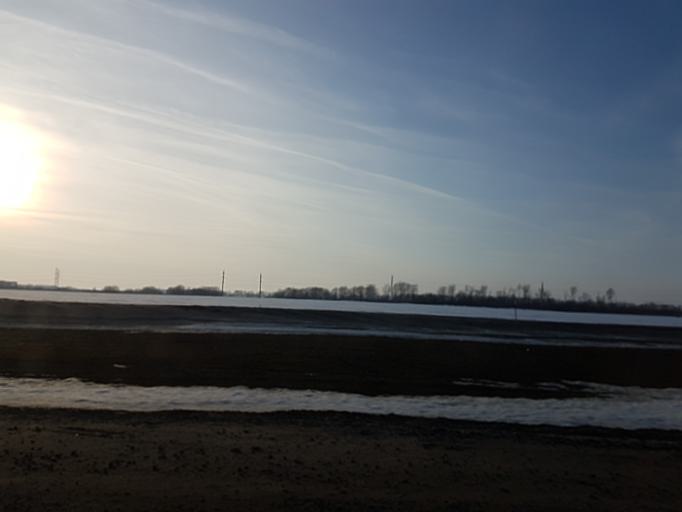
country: RU
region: Tambov
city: Komsomolets
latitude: 52.7464
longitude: 41.2934
